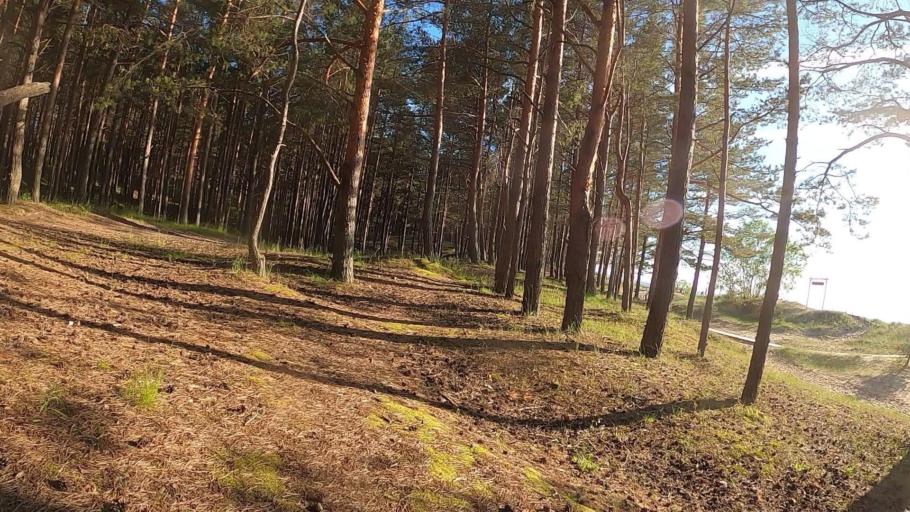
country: LV
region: Riga
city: Jaunciems
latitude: 57.1137
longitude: 24.1912
